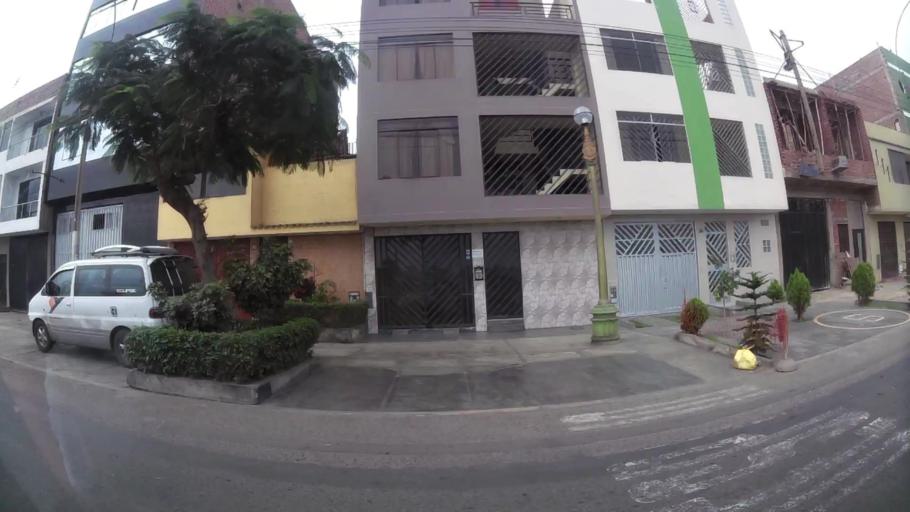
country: PE
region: Callao
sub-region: Callao
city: Callao
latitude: -12.0063
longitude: -77.1077
